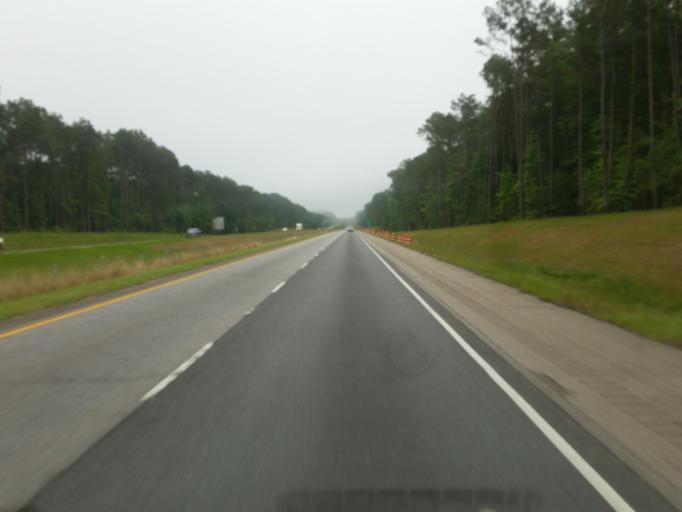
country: US
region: Louisiana
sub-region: Webster Parish
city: Minden
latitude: 32.5672
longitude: -93.1858
